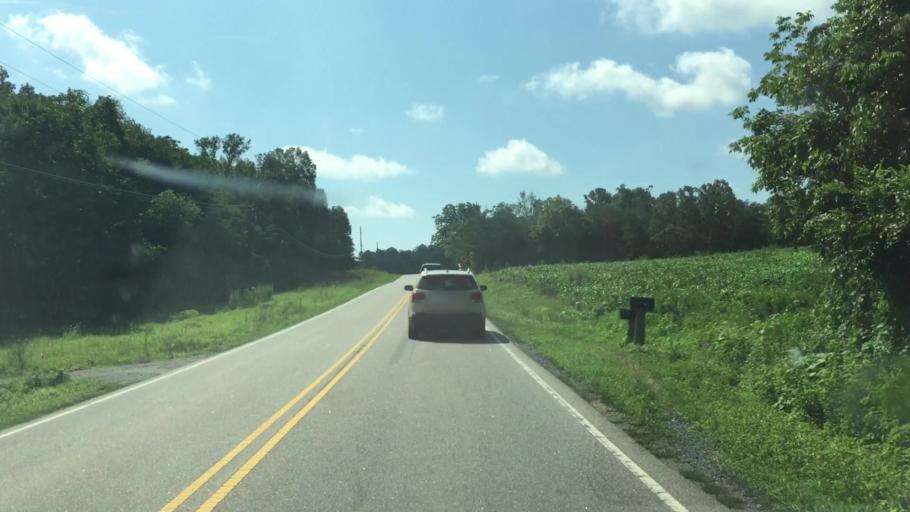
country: US
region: North Carolina
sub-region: Anson County
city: Polkton
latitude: 35.0200
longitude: -80.2228
